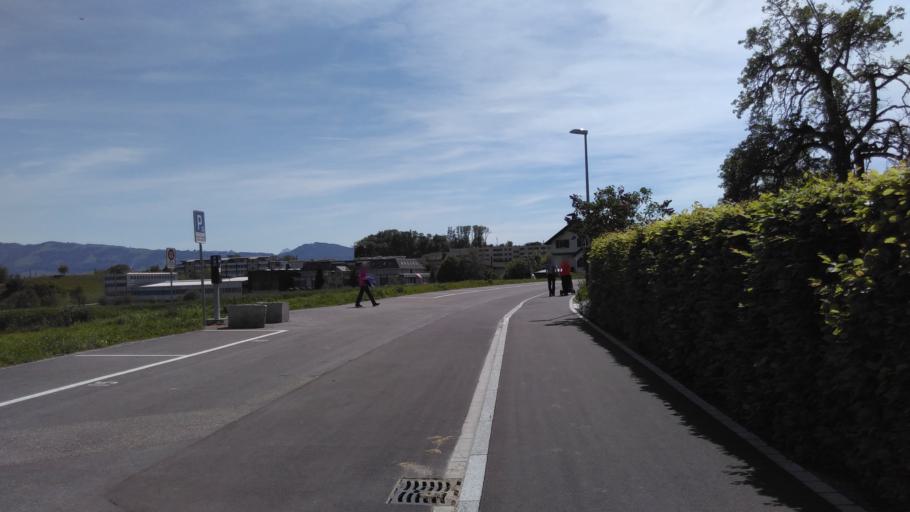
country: CH
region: Zurich
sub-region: Bezirk Hinwil
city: Bubikon
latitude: 47.2731
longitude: 8.8275
